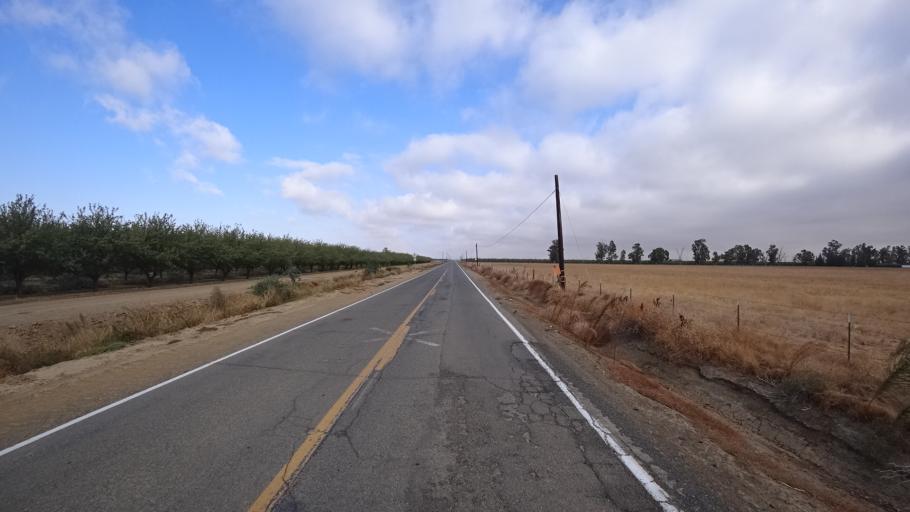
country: US
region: California
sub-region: Yolo County
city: Esparto
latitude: 38.7413
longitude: -122.0075
